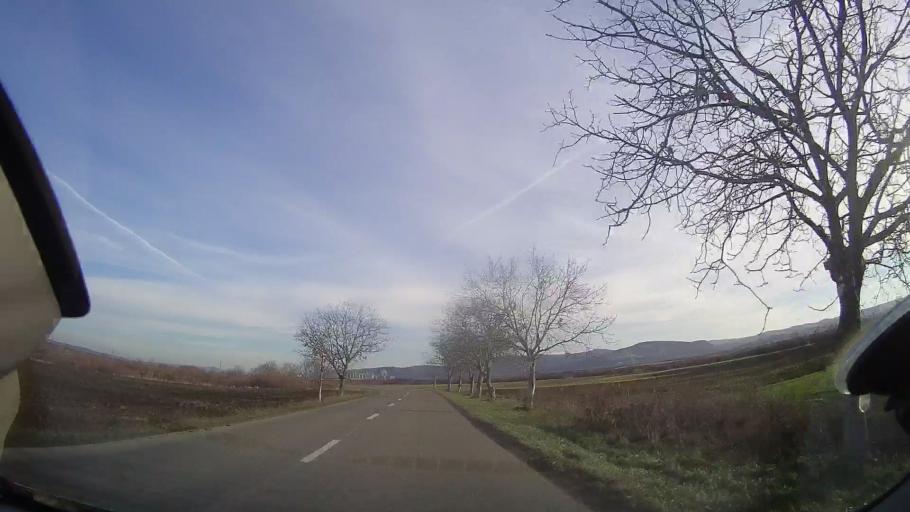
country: RO
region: Bihor
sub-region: Comuna Tetchea
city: Hotar
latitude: 47.0526
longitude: 22.2943
